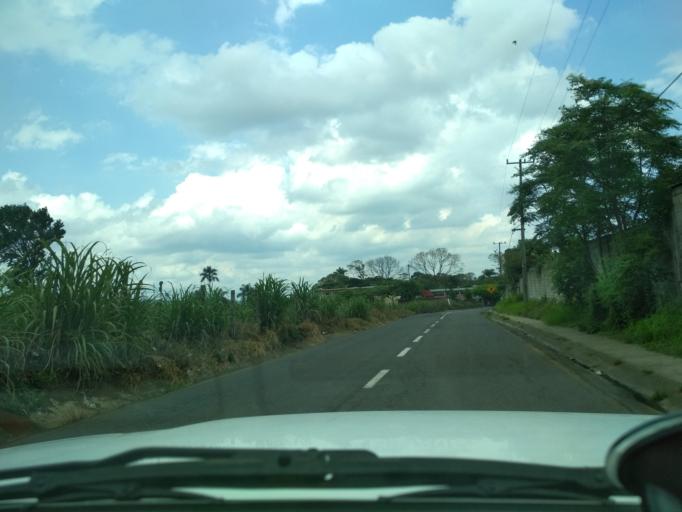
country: MX
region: Veracruz
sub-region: Cordoba
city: San Jose de Abajo [Unidad Habitacional]
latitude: 18.9220
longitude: -96.9637
